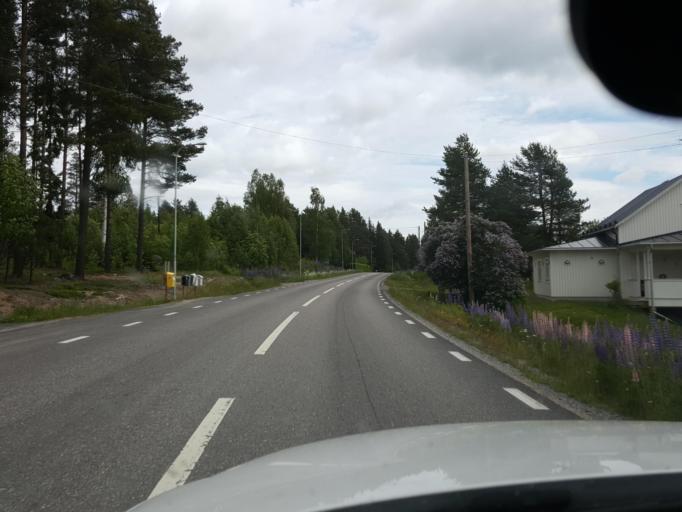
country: SE
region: Gaevleborg
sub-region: Ljusdals Kommun
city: Farila
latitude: 61.7977
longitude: 15.6660
